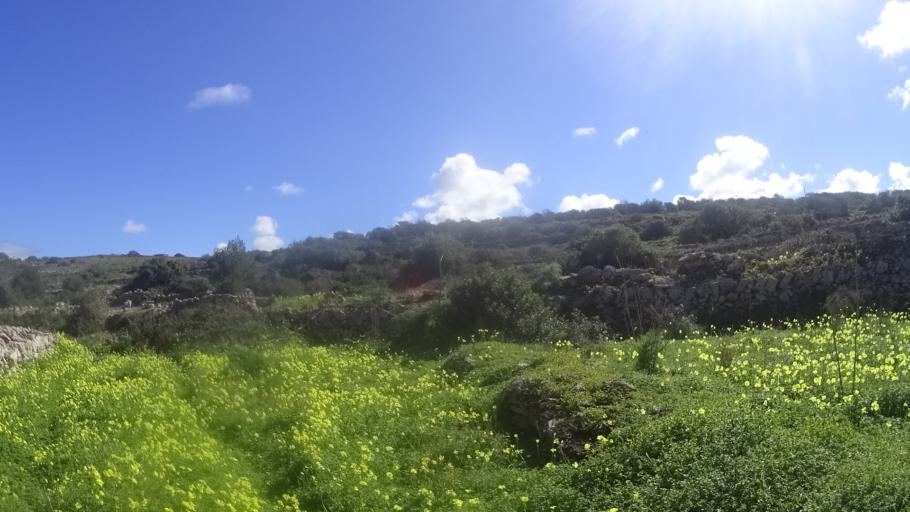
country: MT
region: Il-Mellieha
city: Mellieha
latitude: 35.9511
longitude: 14.3778
